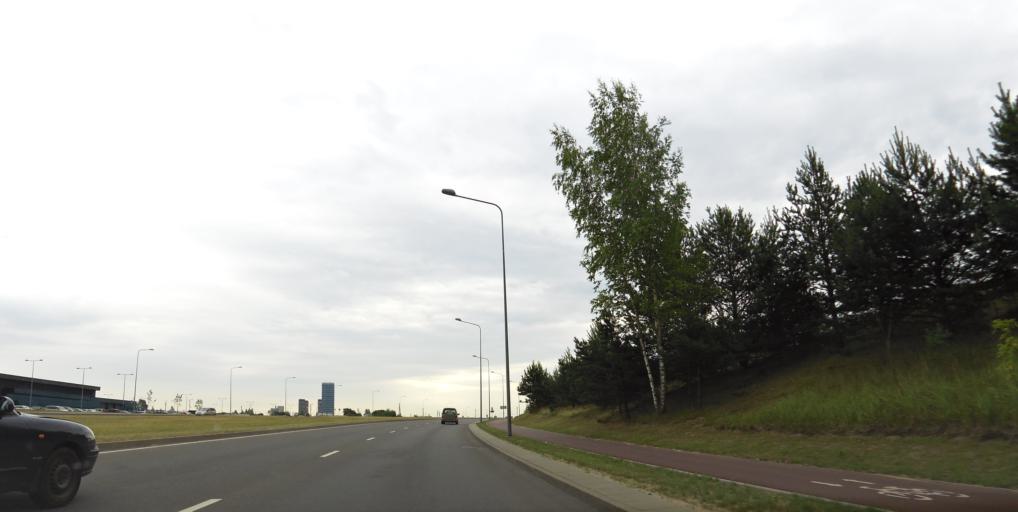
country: LT
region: Vilnius County
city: Pilaite
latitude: 54.7057
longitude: 25.1976
